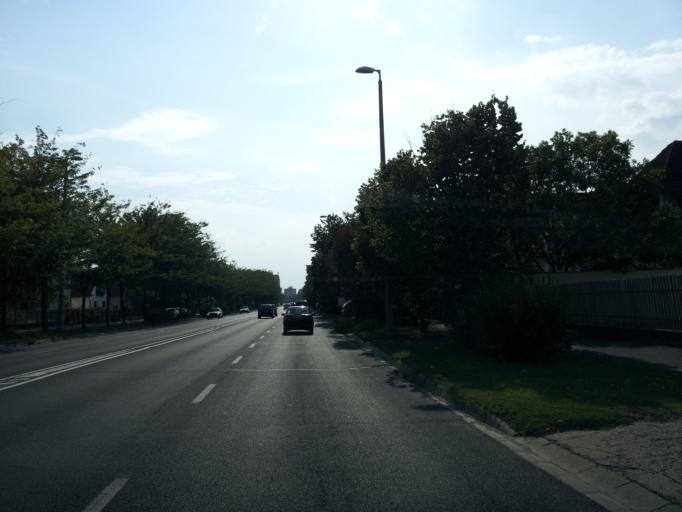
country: HU
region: Somogy
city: Siofok
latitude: 46.9098
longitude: 18.0676
